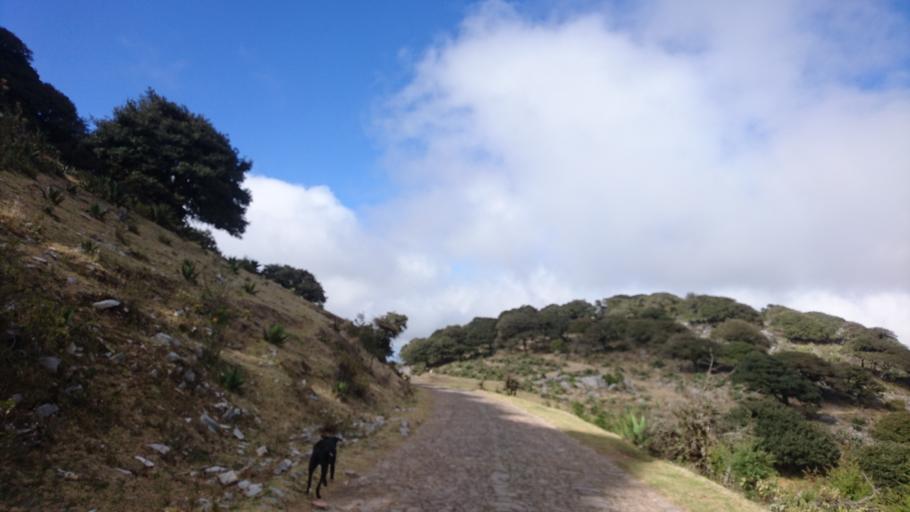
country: MX
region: San Luis Potosi
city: Zaragoza
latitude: 22.0700
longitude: -100.6417
